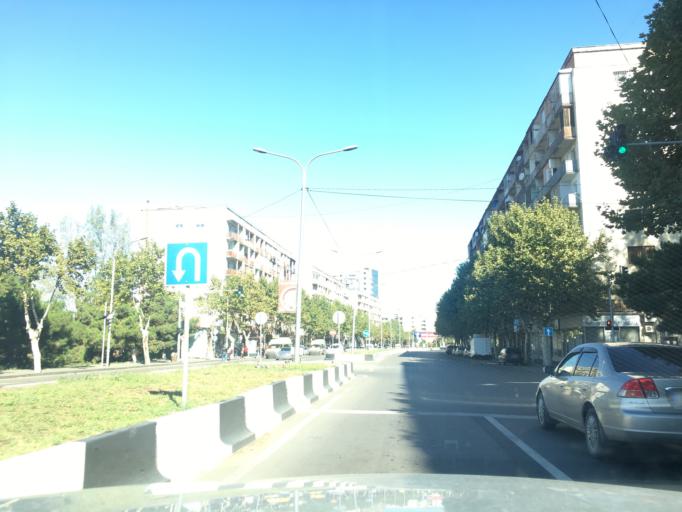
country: GE
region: T'bilisi
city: Tbilisi
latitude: 41.7534
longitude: 44.7891
